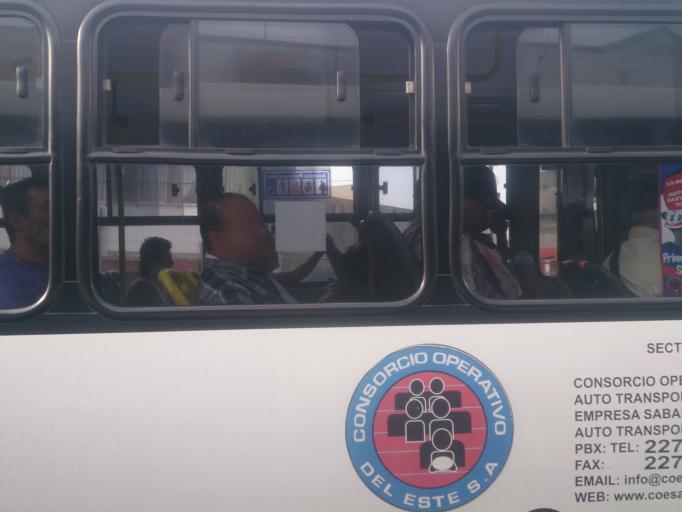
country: CR
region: San Jose
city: San Jose
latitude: 9.9325
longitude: -84.0741
